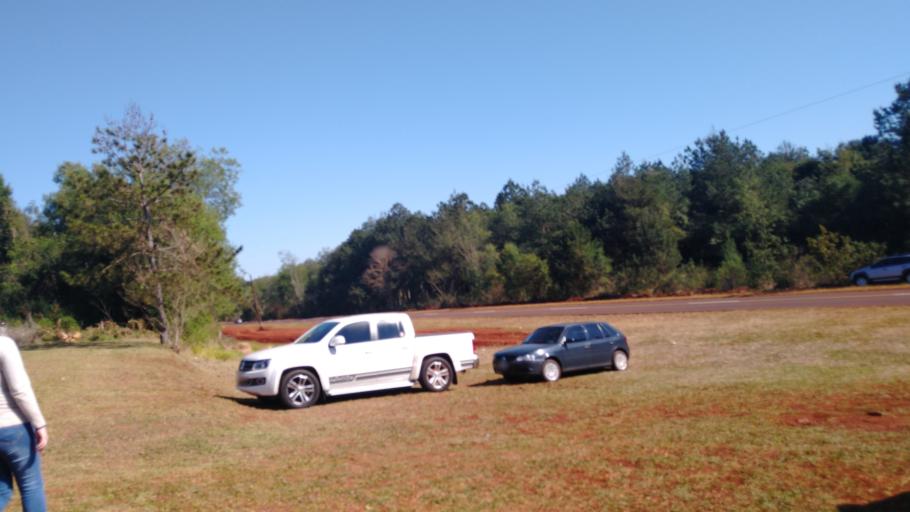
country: AR
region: Misiones
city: Puerto Libertad
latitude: -25.9696
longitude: -54.5412
